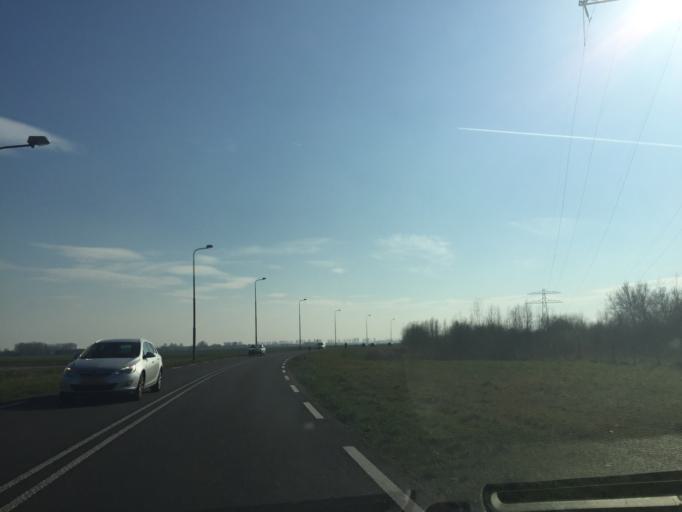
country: NL
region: North Holland
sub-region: Gemeente Bloemendaal
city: Bennebroek
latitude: 52.2960
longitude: 4.6203
